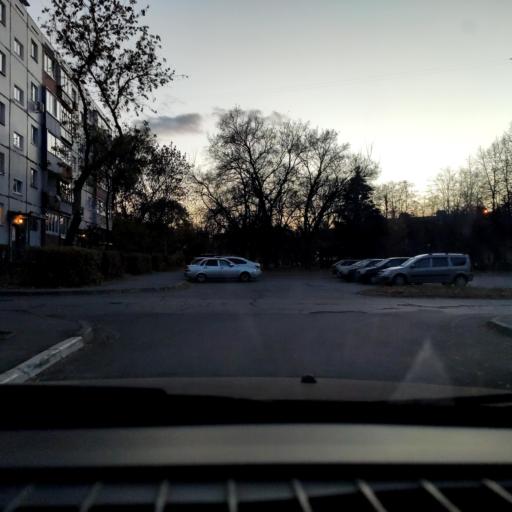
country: RU
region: Samara
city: Tol'yatti
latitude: 53.5127
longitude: 49.2657
